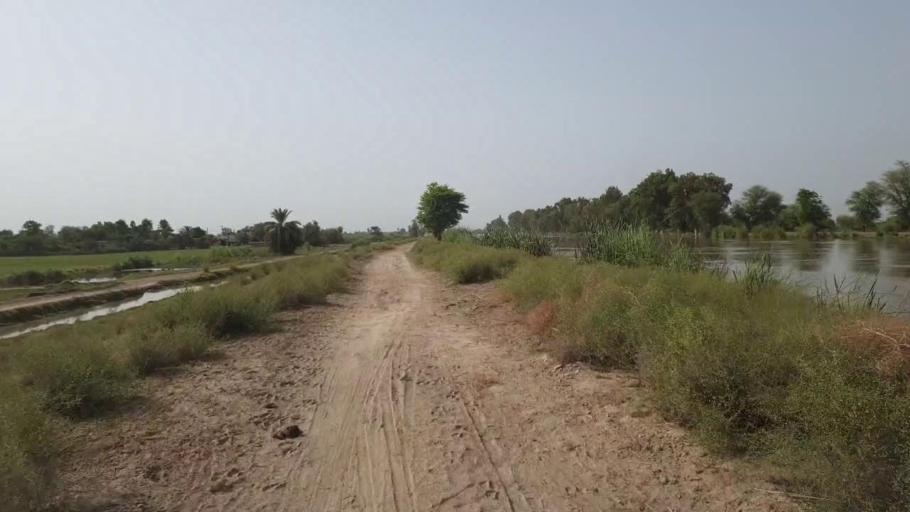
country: PK
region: Sindh
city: Daur
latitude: 26.4491
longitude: 68.1598
